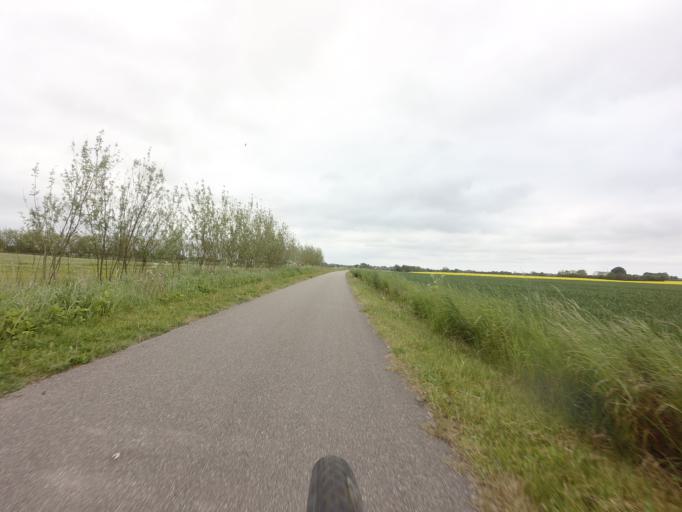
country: DK
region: Zealand
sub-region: Naestved Kommune
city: Fuglebjerg
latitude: 55.2807
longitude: 11.4243
